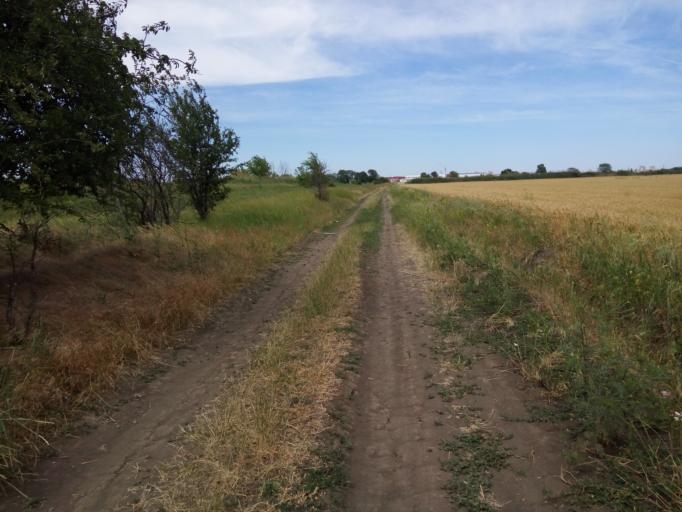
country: RU
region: Rostov
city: Bataysk
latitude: 47.1185
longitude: 39.7228
